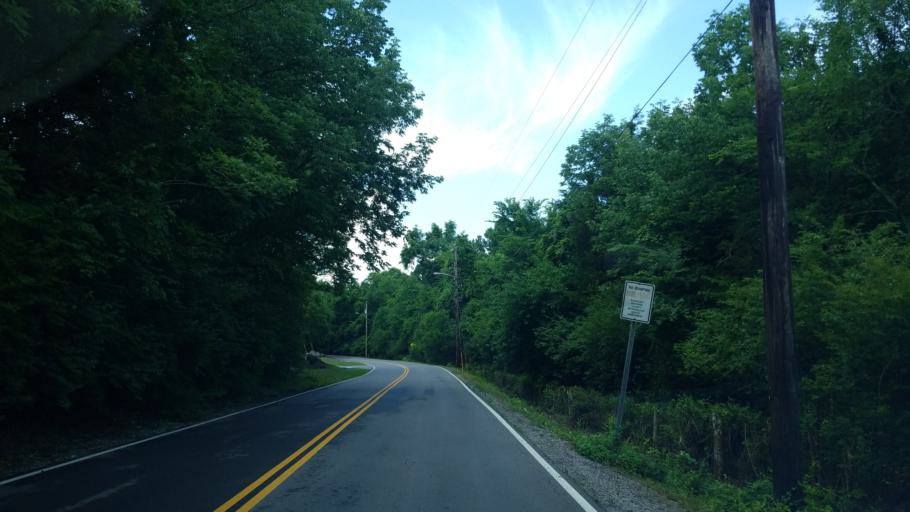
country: US
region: Tennessee
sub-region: Rutherford County
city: La Vergne
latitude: 36.1044
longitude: -86.6325
